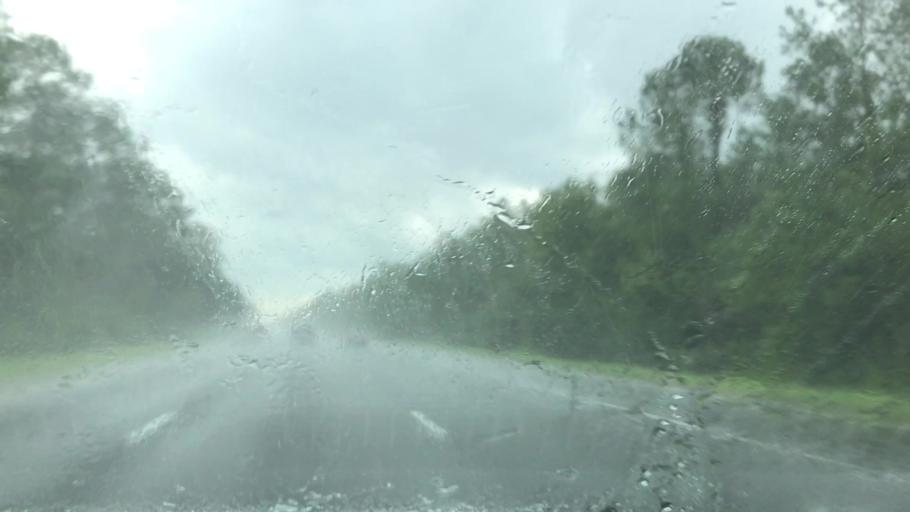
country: US
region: Florida
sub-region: Volusia County
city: Ormond Beach
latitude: 29.2840
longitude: -81.1257
